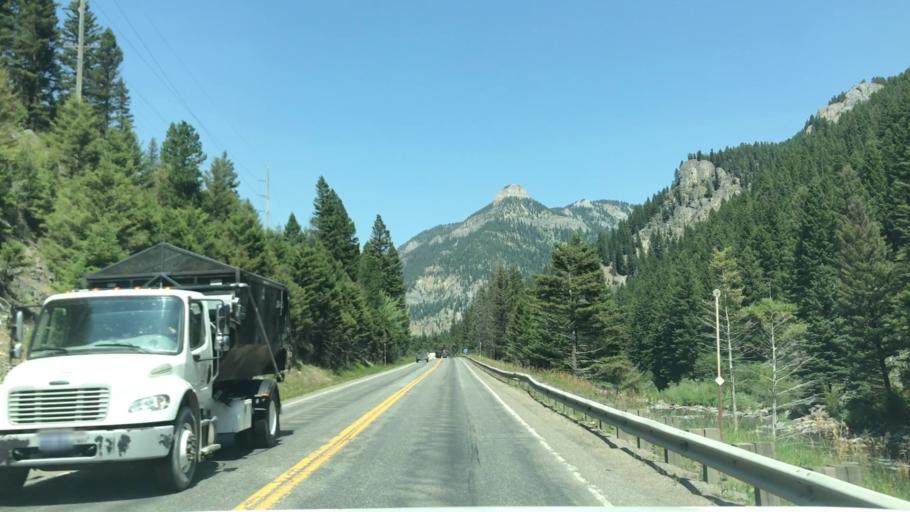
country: US
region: Montana
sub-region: Gallatin County
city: Big Sky
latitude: 45.4253
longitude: -111.2337
